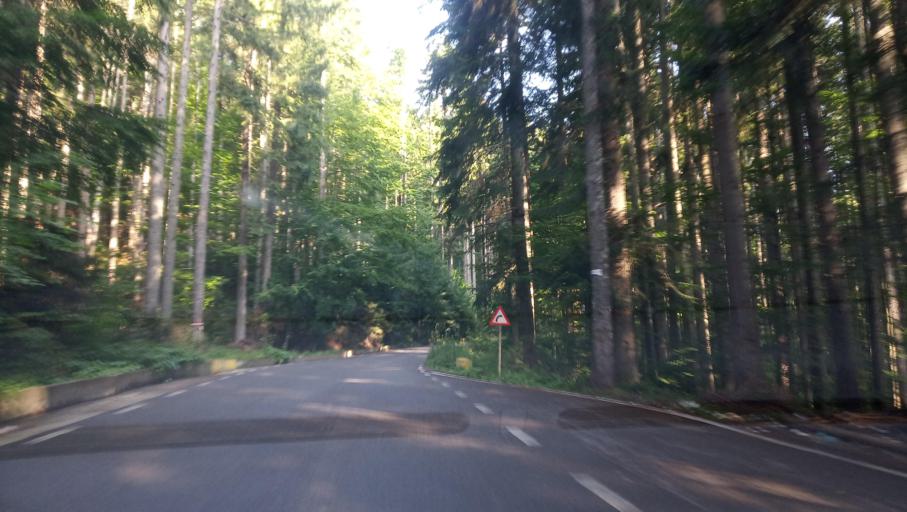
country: RO
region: Prahova
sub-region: Oras Sinaia
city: Sinaia
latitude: 45.3157
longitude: 25.5179
